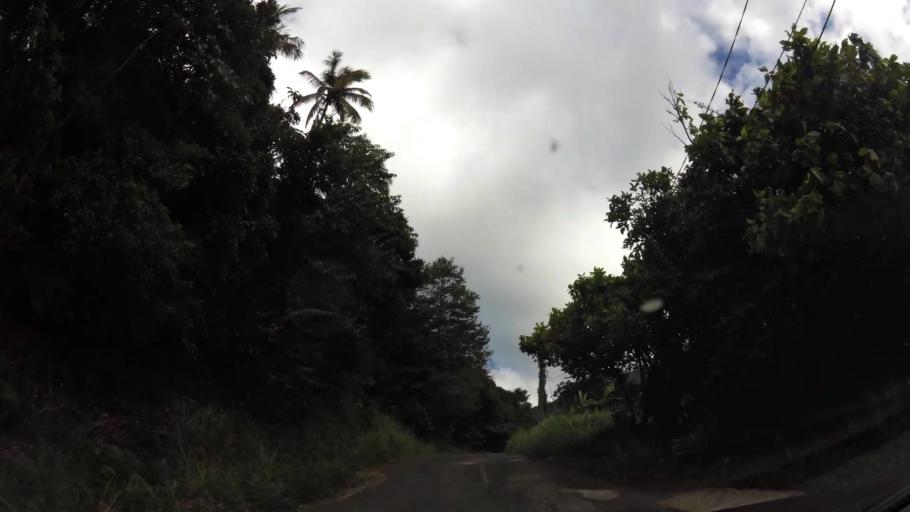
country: DM
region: Saint John
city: Portsmouth
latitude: 15.6069
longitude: -61.4560
